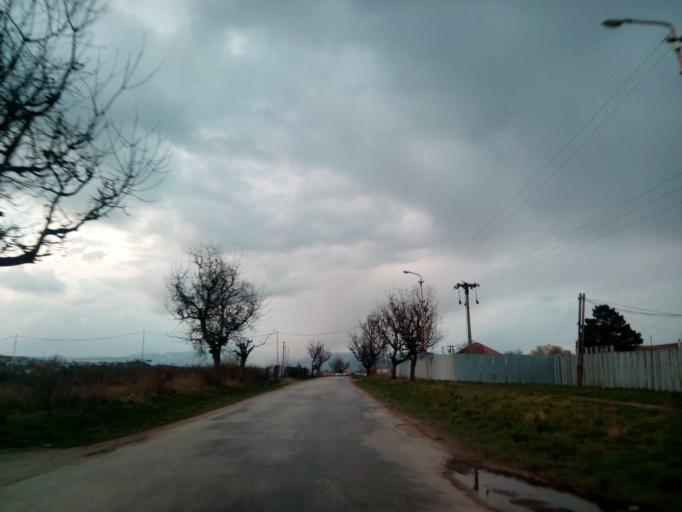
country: SK
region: Kosicky
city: Moldava nad Bodvou
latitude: 48.5987
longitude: 20.9972
